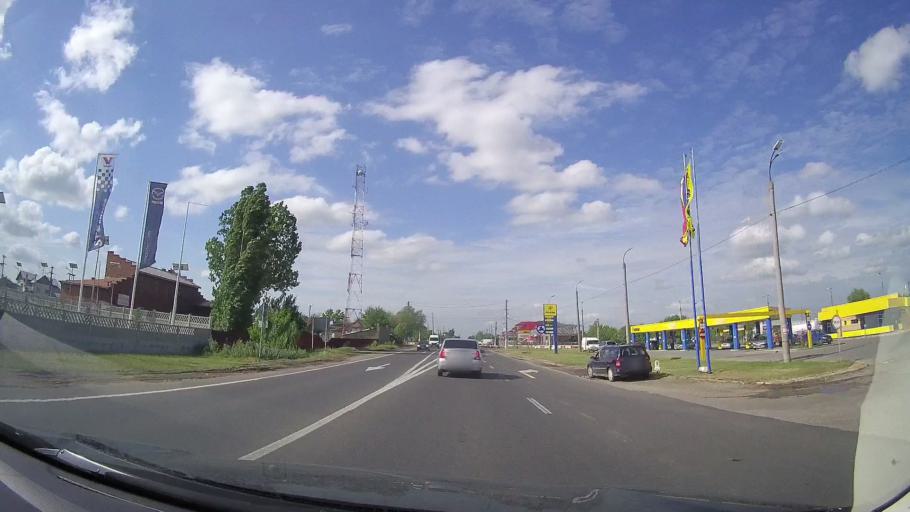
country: RO
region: Giurgiu
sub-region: Comuna Ghimpati
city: Ghimpati
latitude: 44.2045
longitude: 25.7924
